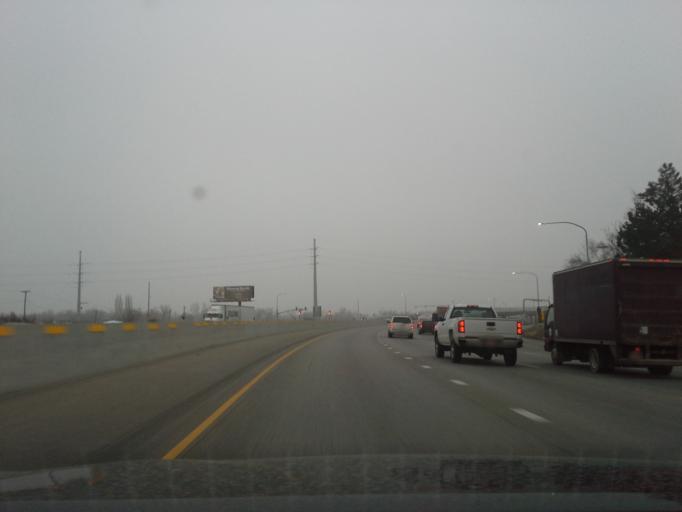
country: US
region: Utah
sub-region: Davis County
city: Layton
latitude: 41.0598
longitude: -111.9629
